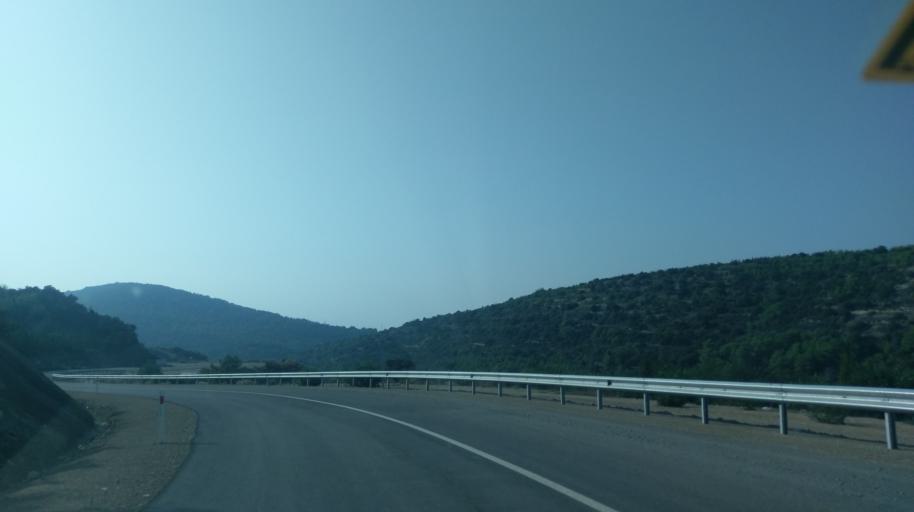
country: CY
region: Ammochostos
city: Leonarisso
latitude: 35.5358
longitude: 34.2567
